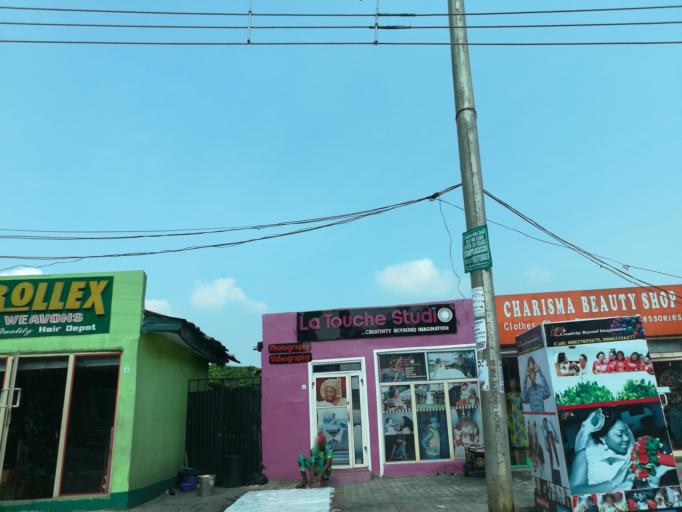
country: NG
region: Rivers
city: Port Harcourt
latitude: 4.8350
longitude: 6.9916
